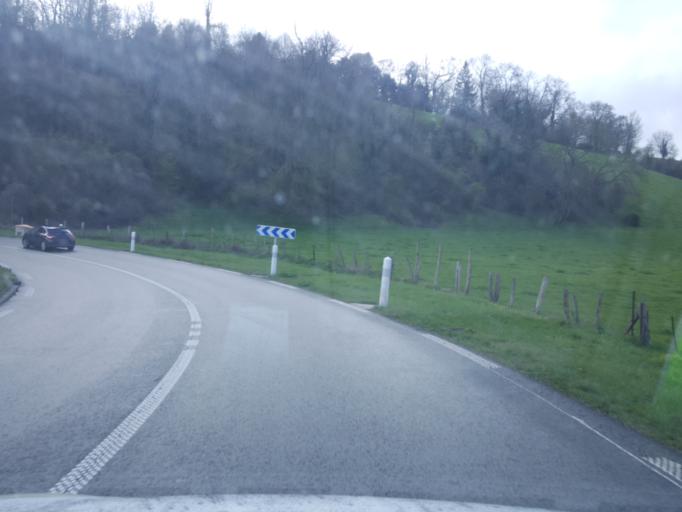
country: FR
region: Picardie
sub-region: Departement de l'Oise
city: Auneuil
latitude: 49.3665
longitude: 1.9792
